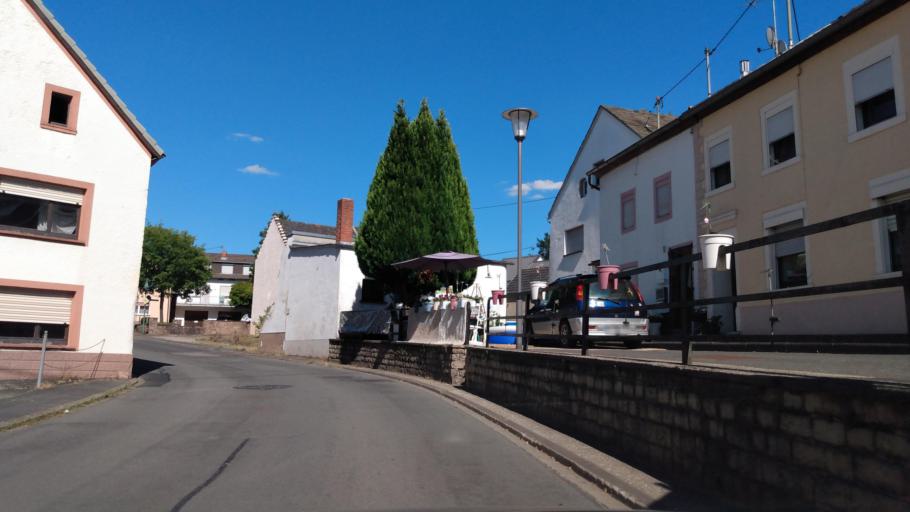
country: DE
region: Rheinland-Pfalz
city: Herforst
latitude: 49.9466
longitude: 6.6962
